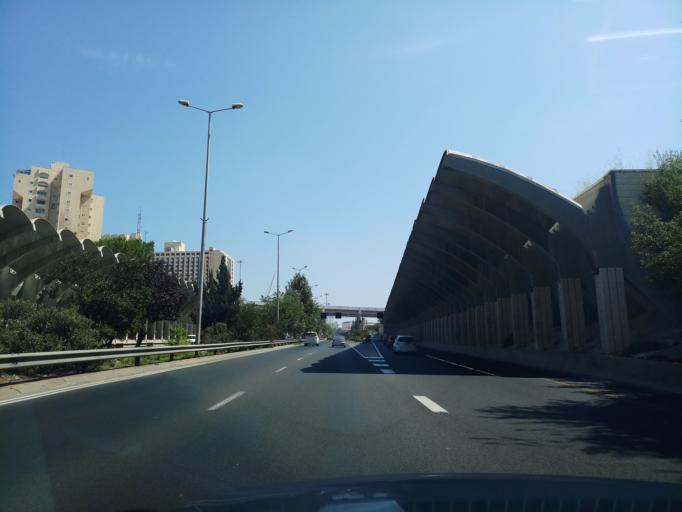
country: IL
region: Jerusalem
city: Jerusalem
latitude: 31.7802
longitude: 35.1955
